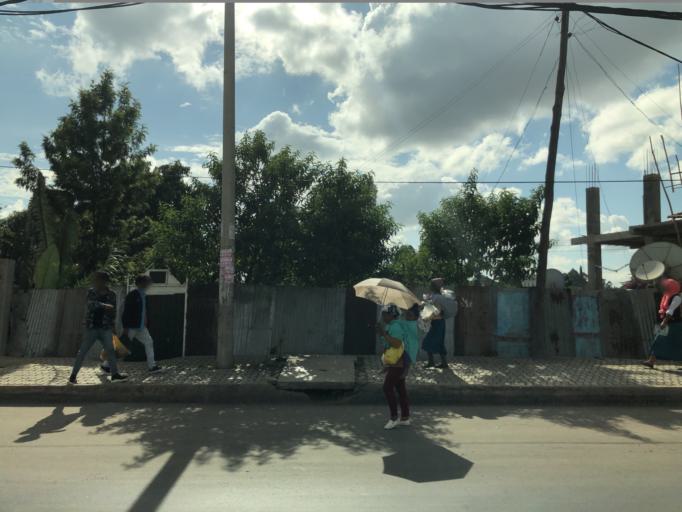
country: ET
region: Adis Abeba
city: Addis Ababa
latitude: 9.0281
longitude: 38.7749
